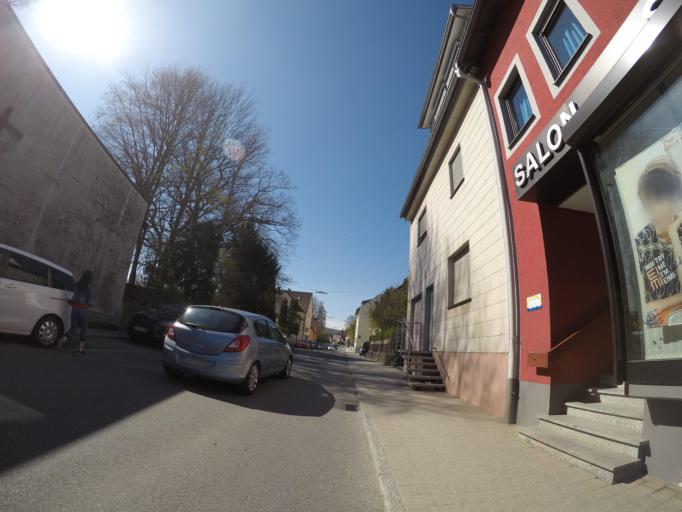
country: DE
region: Baden-Wuerttemberg
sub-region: Tuebingen Region
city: Wilhelmsdorf
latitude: 47.8659
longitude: 9.4245
